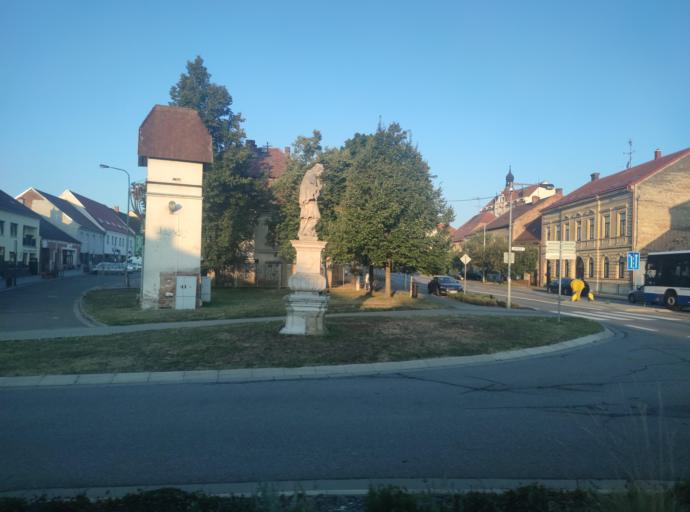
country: CZ
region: South Moravian
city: Rousinov
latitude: 49.2041
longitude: 16.8834
